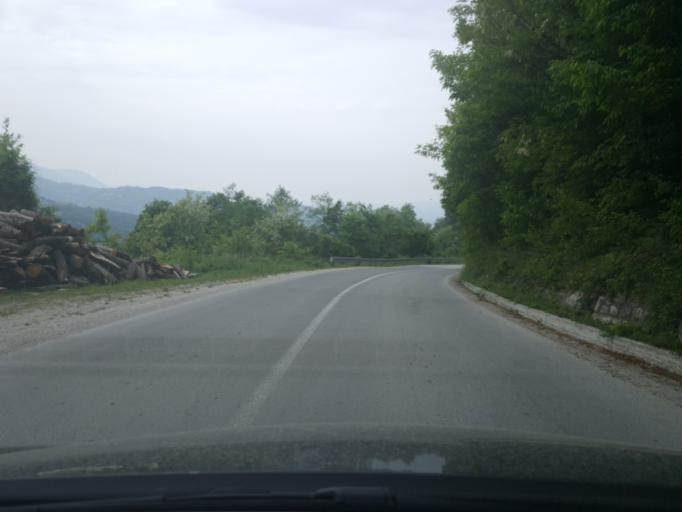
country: RS
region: Central Serbia
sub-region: Zlatiborski Okrug
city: Bajina Basta
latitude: 43.9307
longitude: 19.5715
